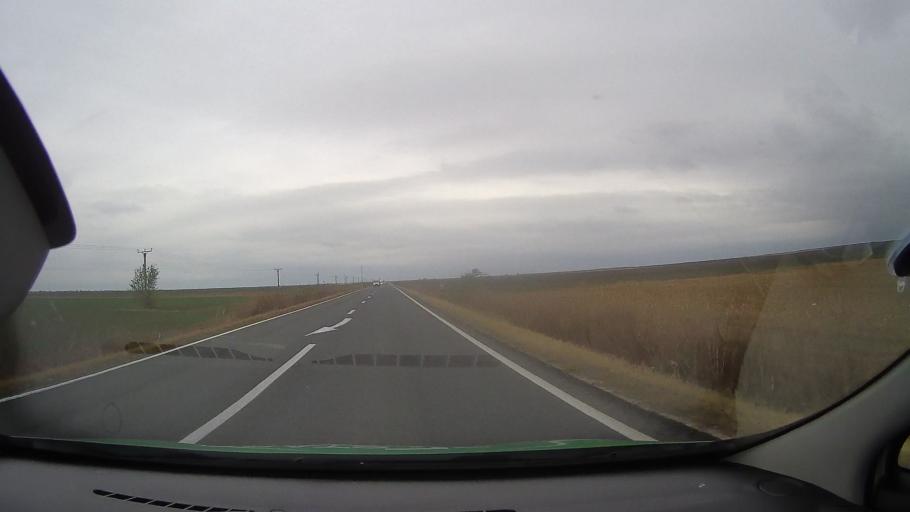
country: RO
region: Constanta
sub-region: Comuna Nicolae Balcescu
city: Nicolae Balcescu
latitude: 44.3795
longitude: 28.4107
